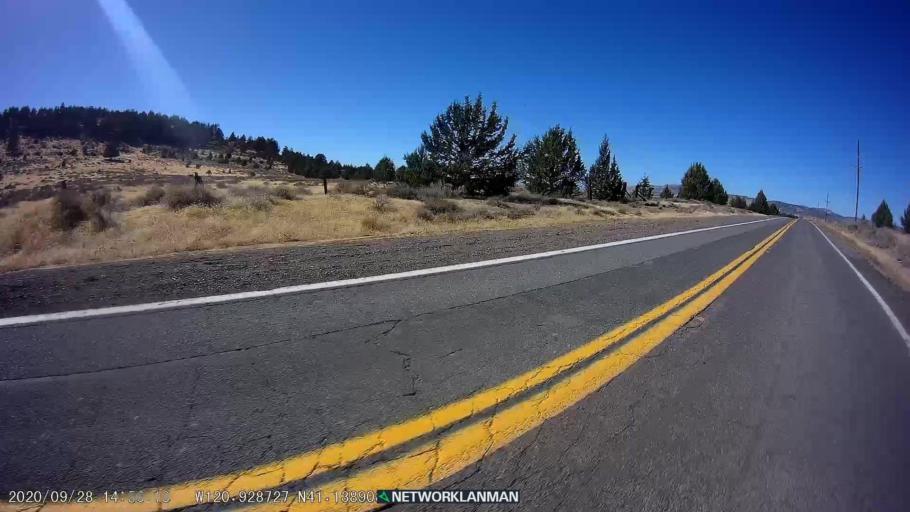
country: US
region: California
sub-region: Modoc County
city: Alturas
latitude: 41.1392
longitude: -120.9288
